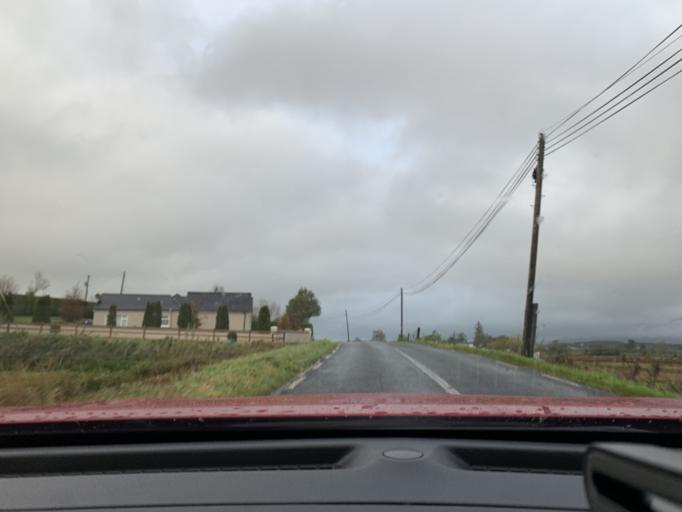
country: IE
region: Connaught
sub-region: Sligo
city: Ballymote
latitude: 54.0148
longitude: -8.5221
